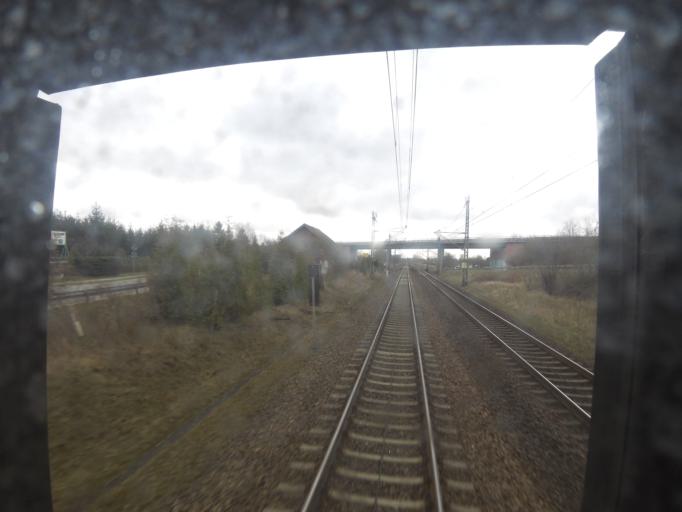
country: DE
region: Mecklenburg-Vorpommern
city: Boizenburg
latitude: 53.3898
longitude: 10.7345
